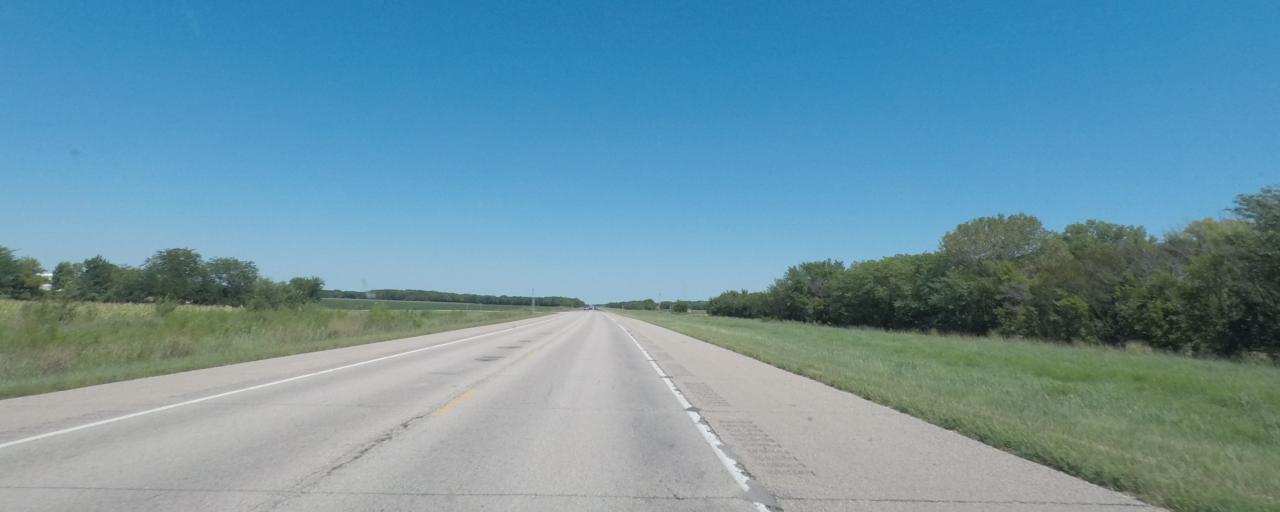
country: US
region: Kansas
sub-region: Chase County
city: Cottonwood Falls
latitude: 38.3033
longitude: -96.7380
